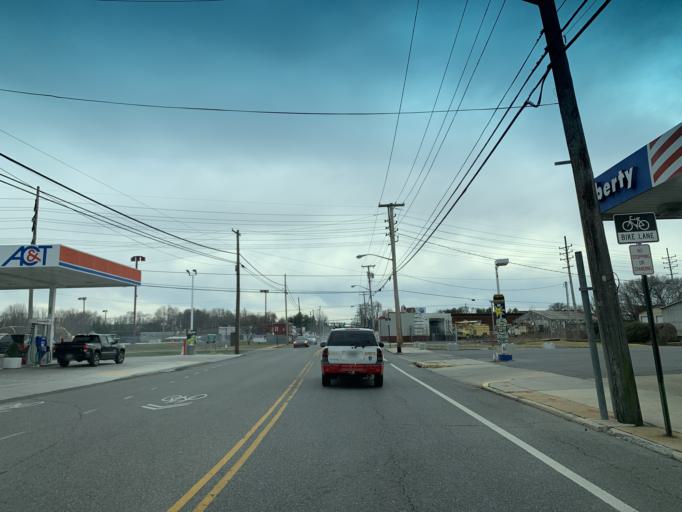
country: US
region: Maryland
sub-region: Washington County
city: Hagerstown
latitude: 39.6282
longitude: -77.7156
